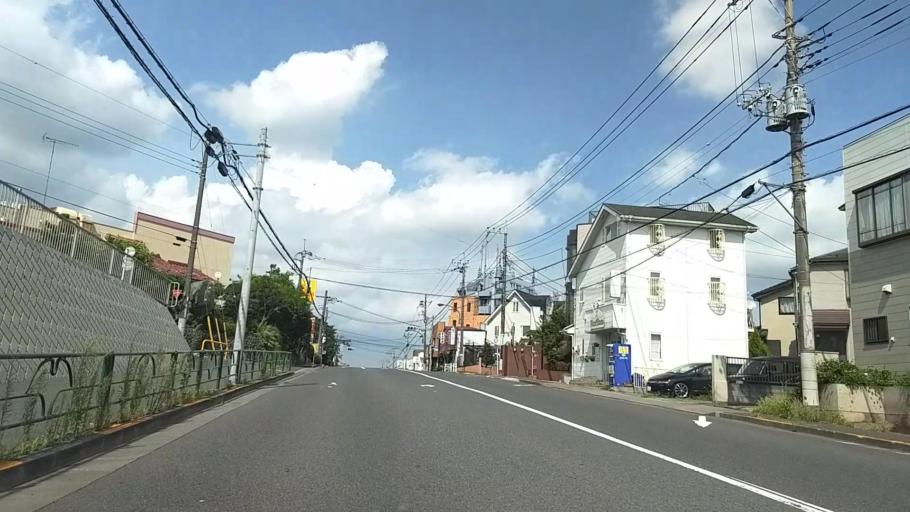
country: JP
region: Tokyo
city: Hachioji
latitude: 35.6494
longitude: 139.3229
